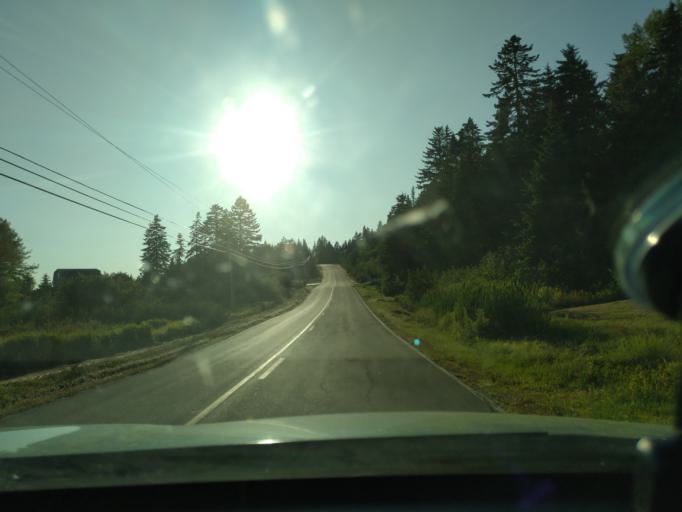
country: US
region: Maine
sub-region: Washington County
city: Machiasport
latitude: 44.6590
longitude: -67.2158
